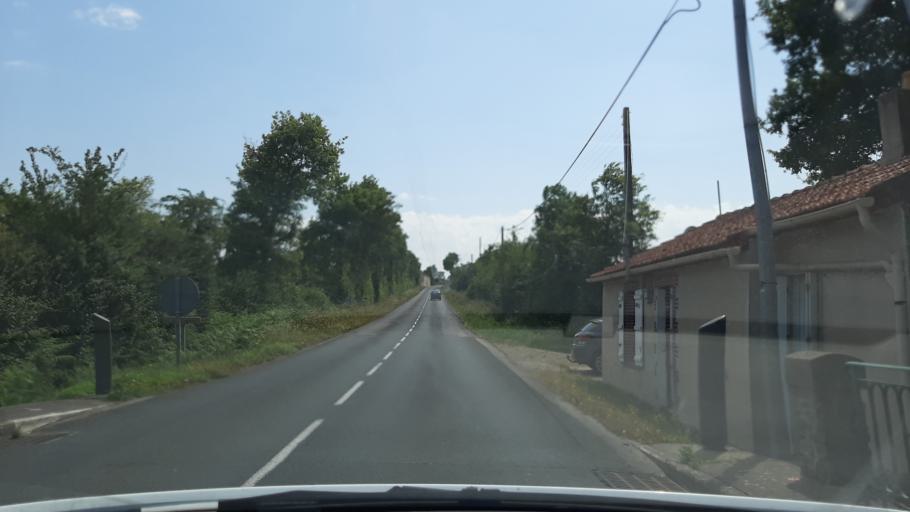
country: FR
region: Pays de la Loire
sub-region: Departement de la Vendee
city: Le Poire-sur-Vie
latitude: 46.7825
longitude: -1.5309
